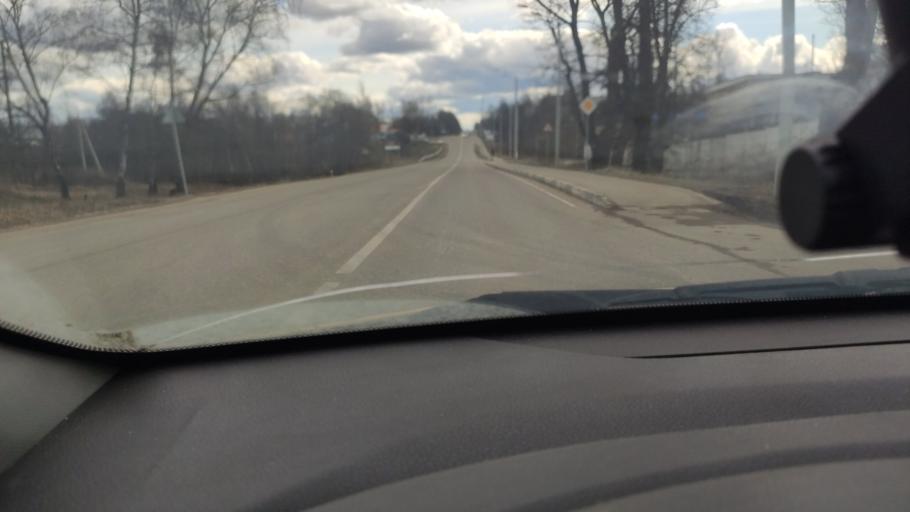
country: RU
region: Moskovskaya
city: Ruza
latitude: 55.7108
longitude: 36.1789
